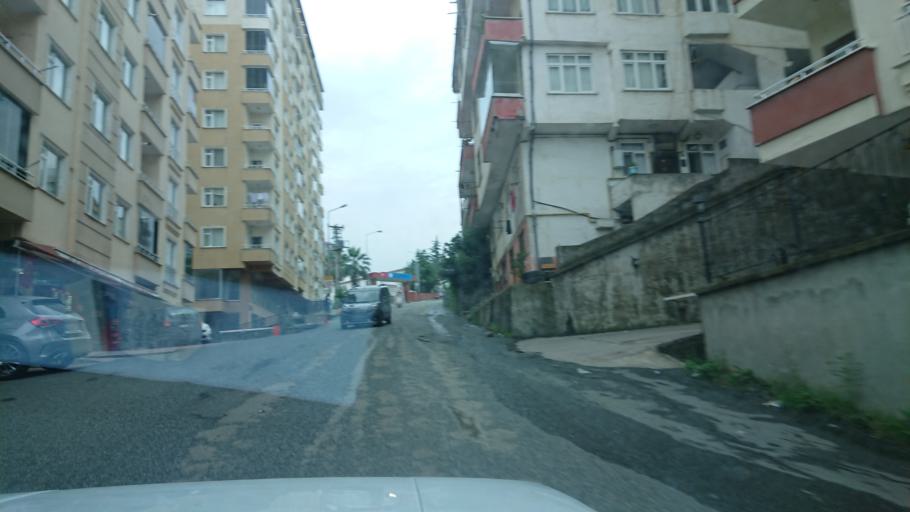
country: TR
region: Rize
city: Rize
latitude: 41.0172
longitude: 40.5141
